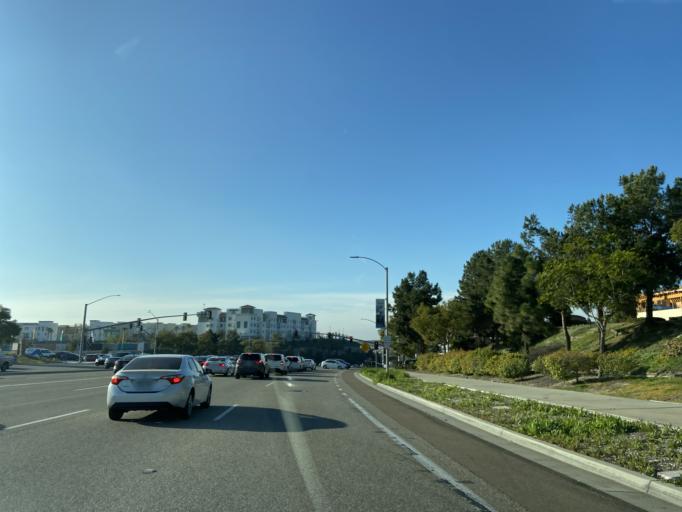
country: US
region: California
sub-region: San Diego County
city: Bonita
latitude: 32.6282
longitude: -116.9662
